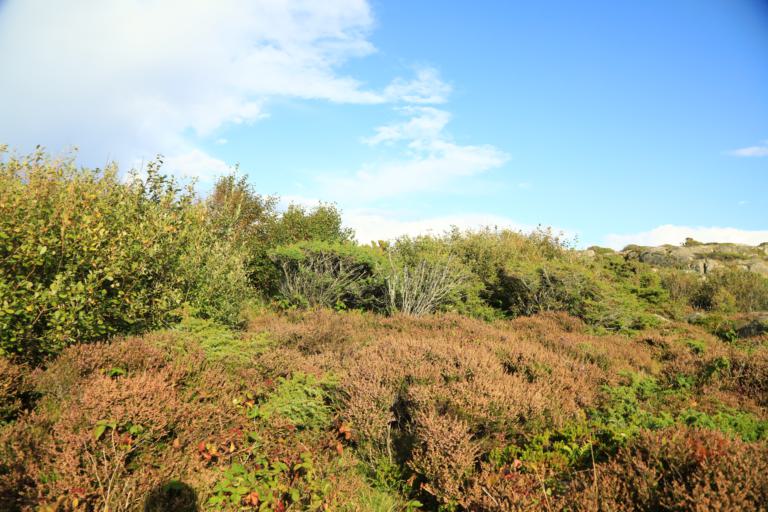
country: SE
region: Halland
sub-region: Varbergs Kommun
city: Varberg
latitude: 57.1178
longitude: 12.1950
